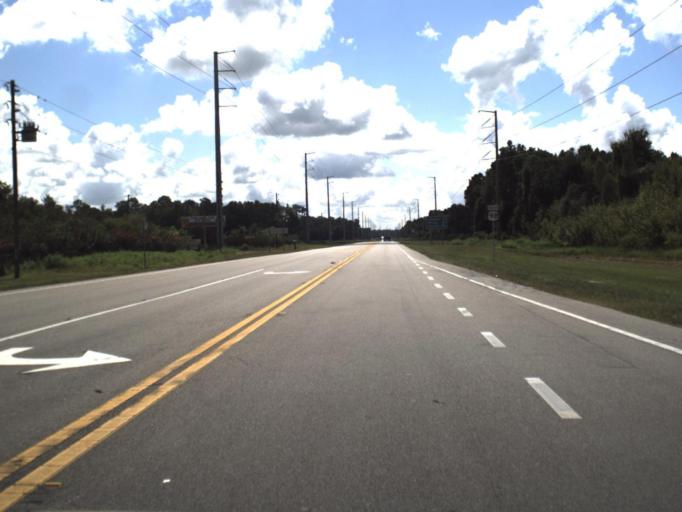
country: US
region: Florida
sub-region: Pasco County
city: Zephyrhills North
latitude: 28.2591
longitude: -82.0755
